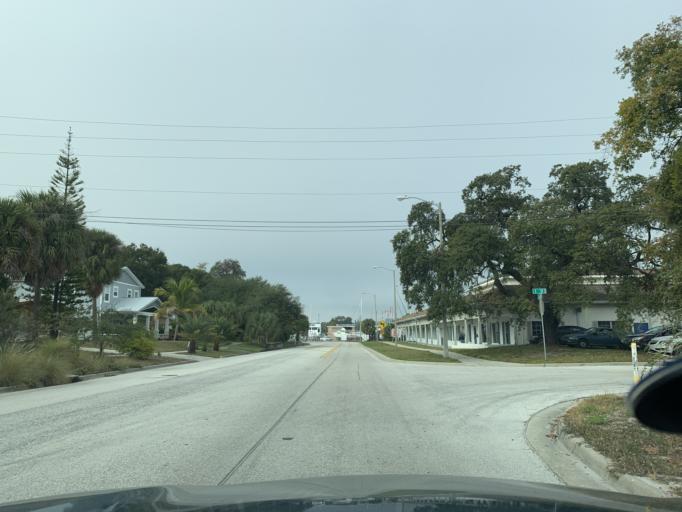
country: US
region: Florida
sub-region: Pinellas County
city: Saint Petersburg
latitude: 27.7548
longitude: -82.6336
